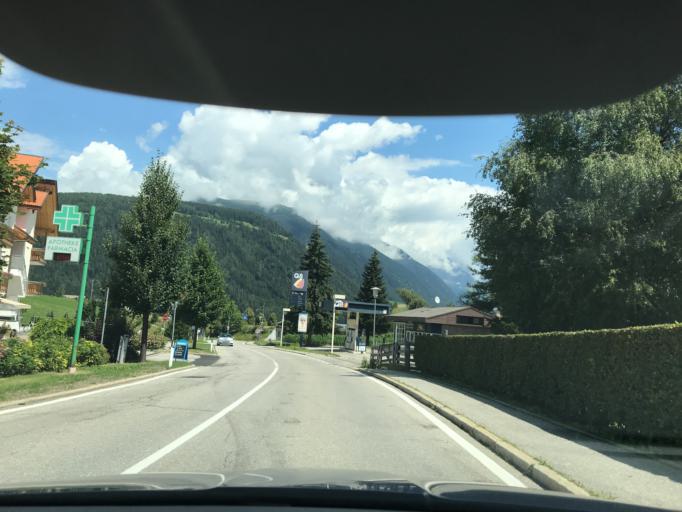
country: IT
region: Trentino-Alto Adige
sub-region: Bolzano
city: Valdaora di Mezzo
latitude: 46.7625
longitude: 12.0317
